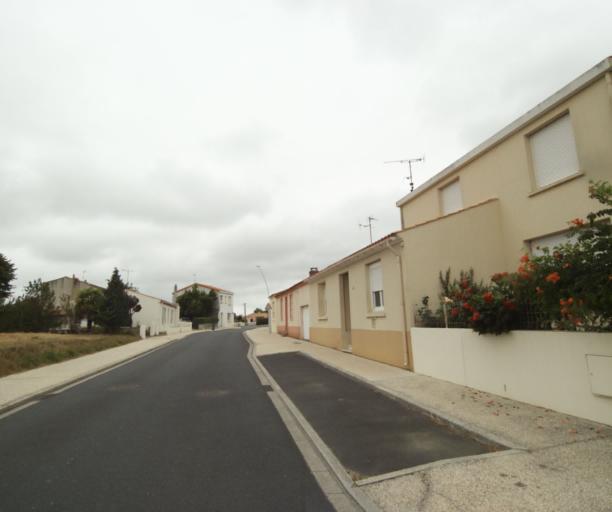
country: FR
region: Pays de la Loire
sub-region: Departement de la Vendee
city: Chateau-d'Olonne
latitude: 46.5056
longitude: -1.7407
